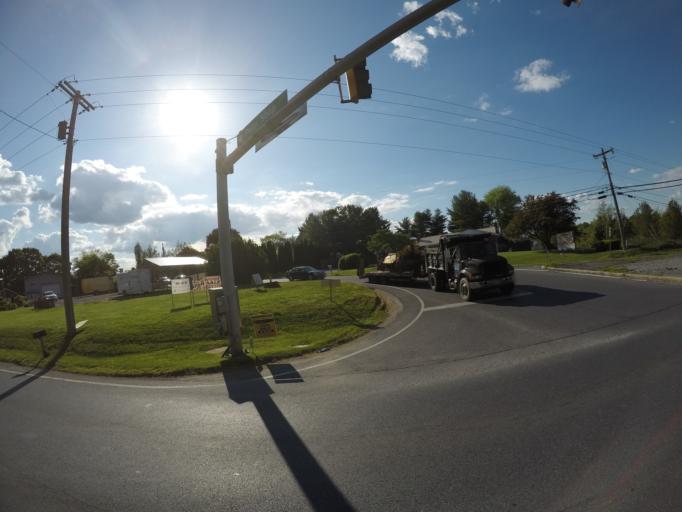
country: US
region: Maryland
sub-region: Carroll County
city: Mount Airy
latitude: 39.3514
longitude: -77.1694
